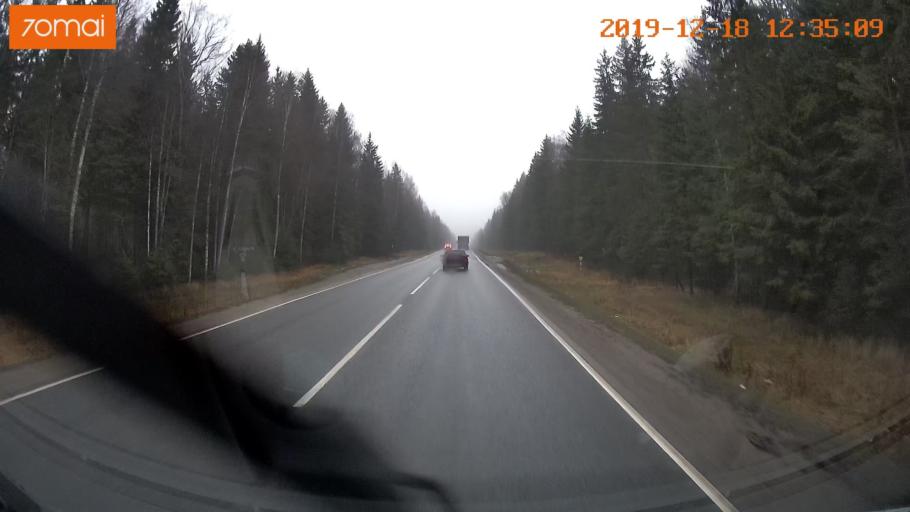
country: RU
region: Moskovskaya
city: Rumyantsevo
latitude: 56.1267
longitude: 36.5796
